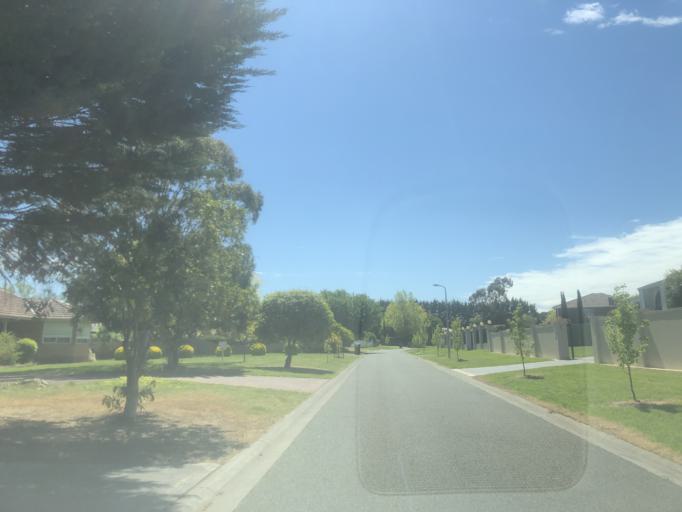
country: AU
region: Victoria
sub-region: Casey
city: Endeavour Hills
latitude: -37.9812
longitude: 145.2854
